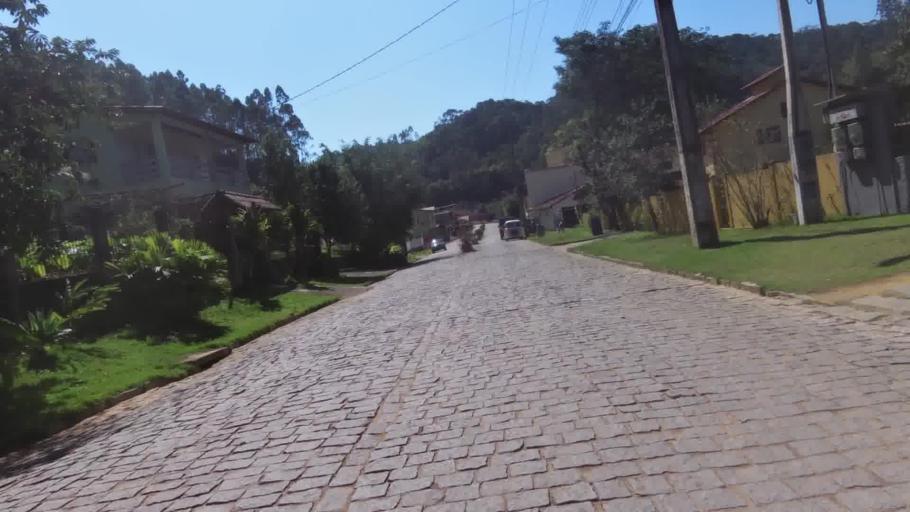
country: BR
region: Espirito Santo
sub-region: Alfredo Chaves
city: Alfredo Chaves
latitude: -20.5545
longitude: -40.8154
